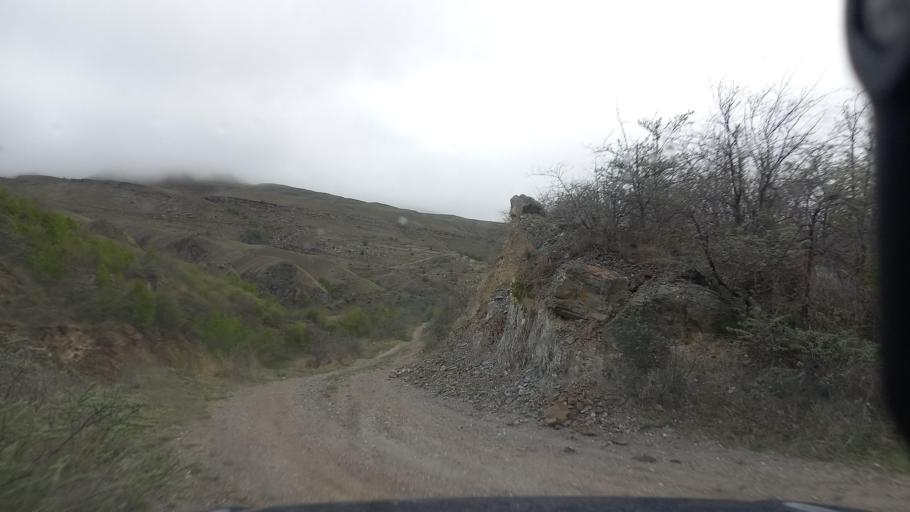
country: RU
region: Kabardino-Balkariya
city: Bylym
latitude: 43.4562
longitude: 43.0034
